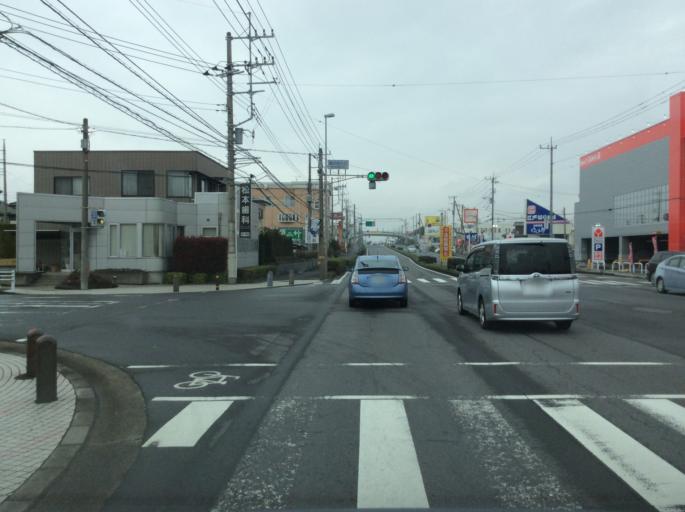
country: JP
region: Ibaraki
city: Mitsukaido
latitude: 35.9775
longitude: 139.9826
